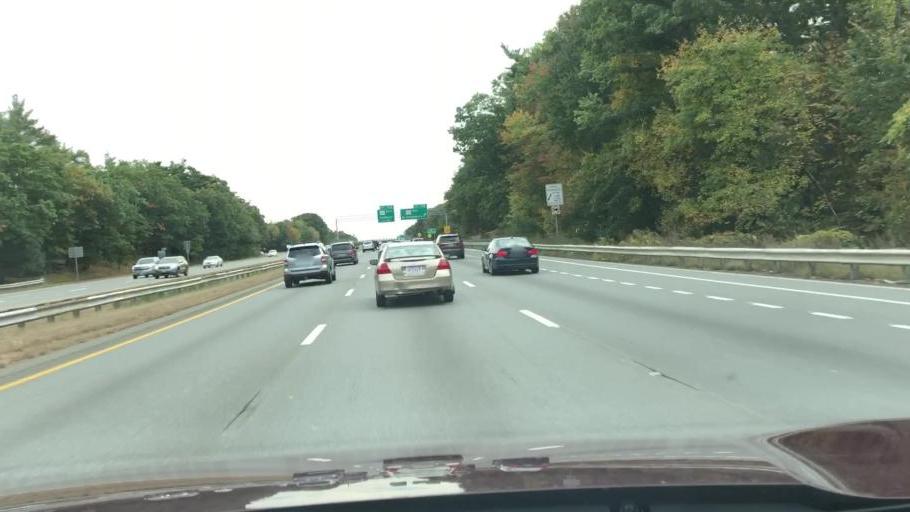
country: US
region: Massachusetts
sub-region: Essex County
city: Andover
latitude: 42.6509
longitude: -71.1884
